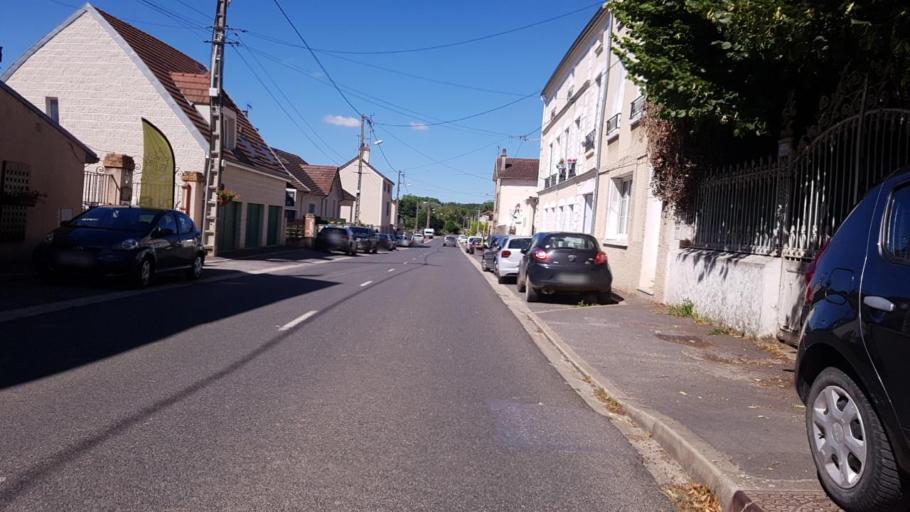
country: FR
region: Ile-de-France
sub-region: Departement de Seine-et-Marne
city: Saacy-sur-Marne
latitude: 48.9790
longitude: 3.2372
